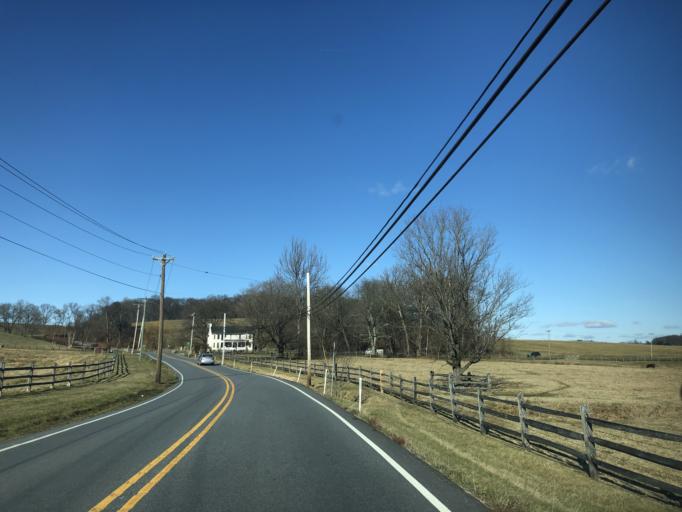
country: US
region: Pennsylvania
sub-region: Chester County
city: South Coatesville
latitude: 39.9210
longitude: -75.8213
